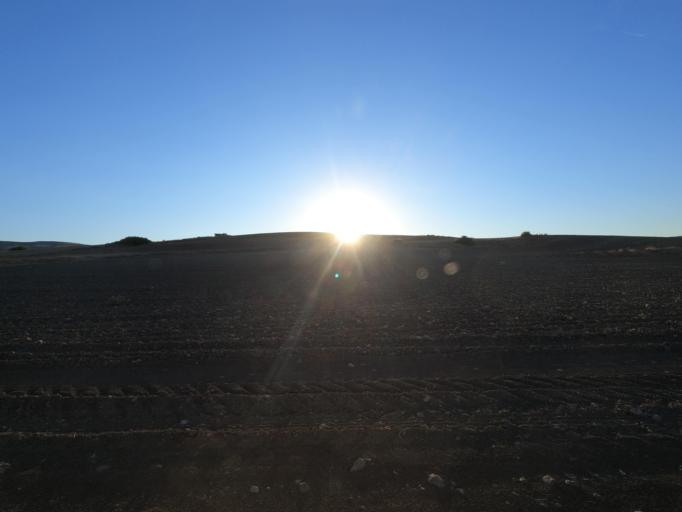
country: CY
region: Larnaka
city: Troulloi
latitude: 35.0264
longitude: 33.6312
